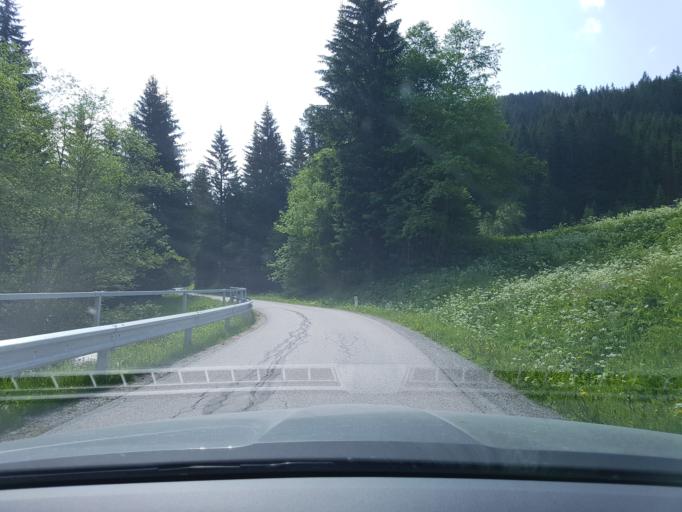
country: AT
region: Salzburg
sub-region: Politischer Bezirk Tamsweg
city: Thomatal
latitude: 47.0383
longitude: 13.7149
